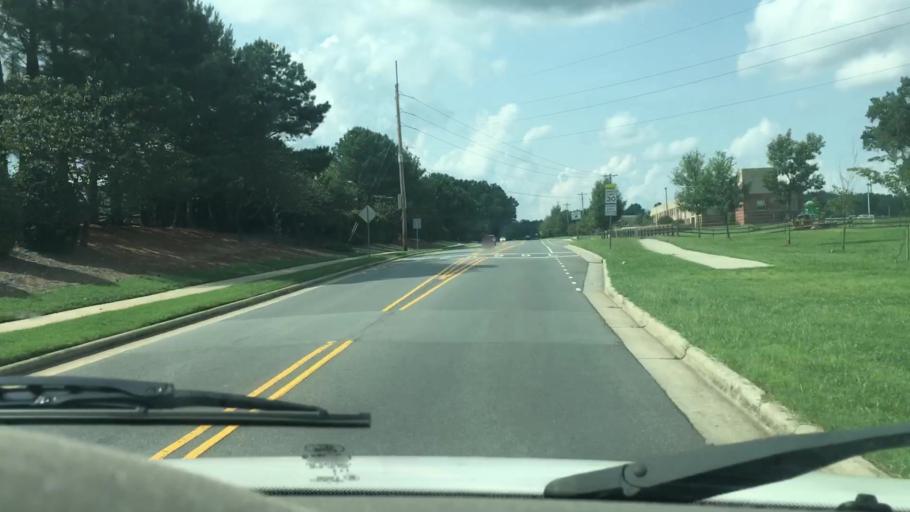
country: US
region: North Carolina
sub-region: Mecklenburg County
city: Huntersville
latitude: 35.4237
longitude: -80.8711
